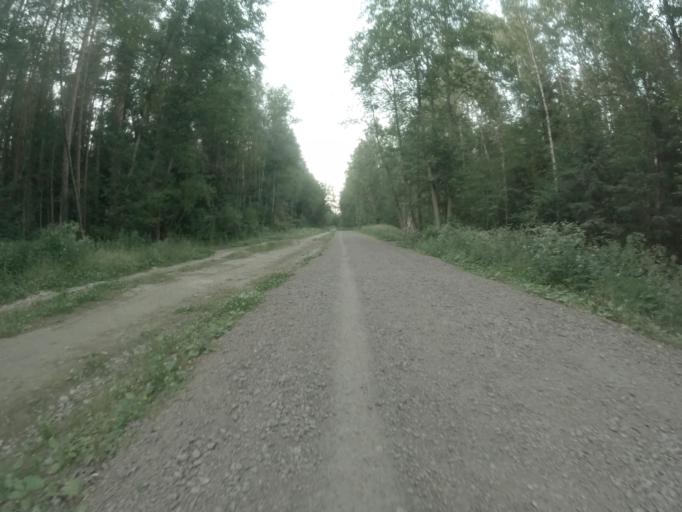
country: RU
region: St.-Petersburg
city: Krasnogvargeisky
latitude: 59.9554
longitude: 30.5187
